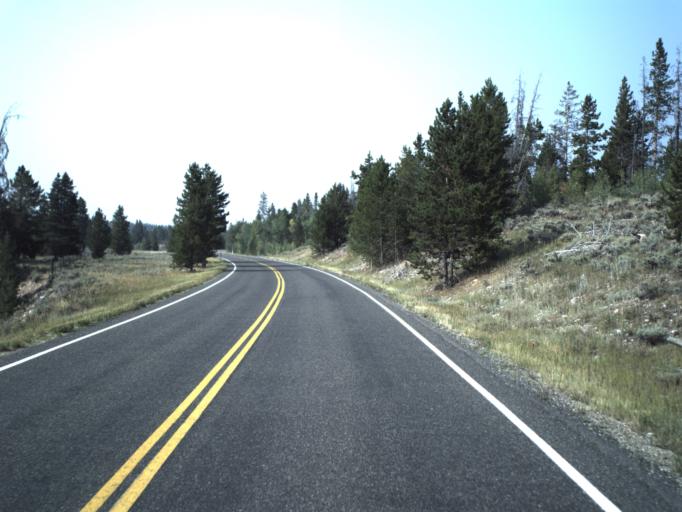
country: US
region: Wyoming
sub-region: Uinta County
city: Evanston
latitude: 40.8879
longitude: -110.8315
